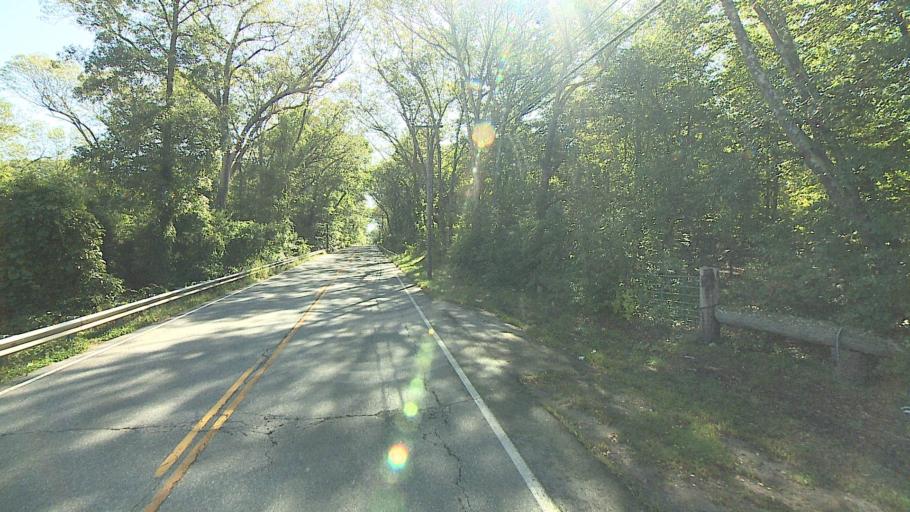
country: US
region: Connecticut
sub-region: New London County
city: Norwich
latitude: 41.5572
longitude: -72.0383
